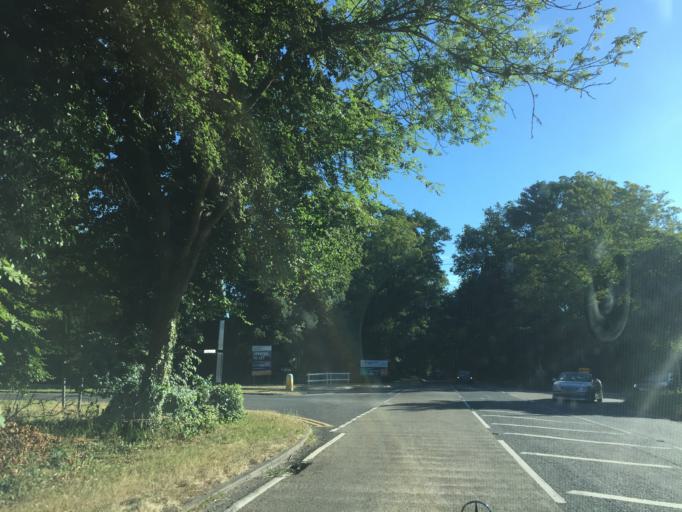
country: GB
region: England
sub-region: Warwickshire
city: Royal Leamington Spa
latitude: 52.3378
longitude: -1.5184
